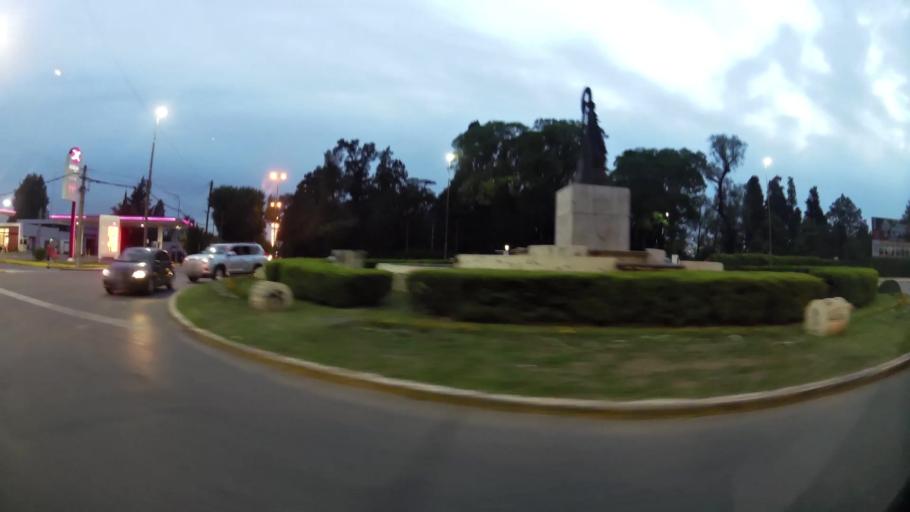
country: AR
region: Santa Fe
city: Funes
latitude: -32.9282
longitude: -60.7390
